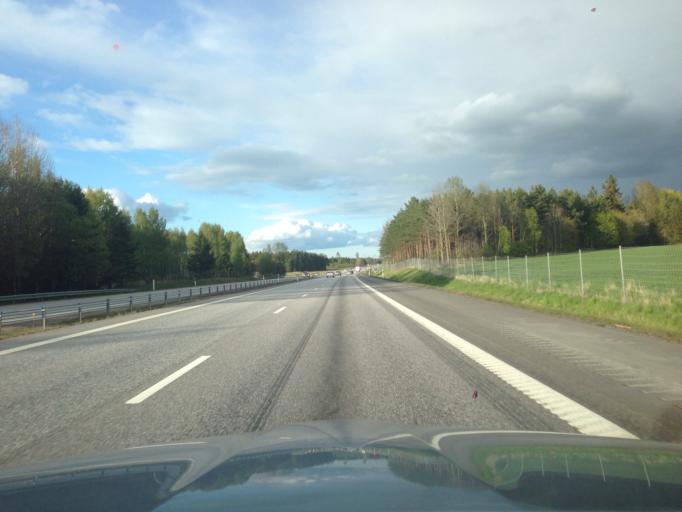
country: SE
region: OEstergoetland
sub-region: Linkopings Kommun
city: Vikingstad
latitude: 58.3990
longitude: 15.4321
